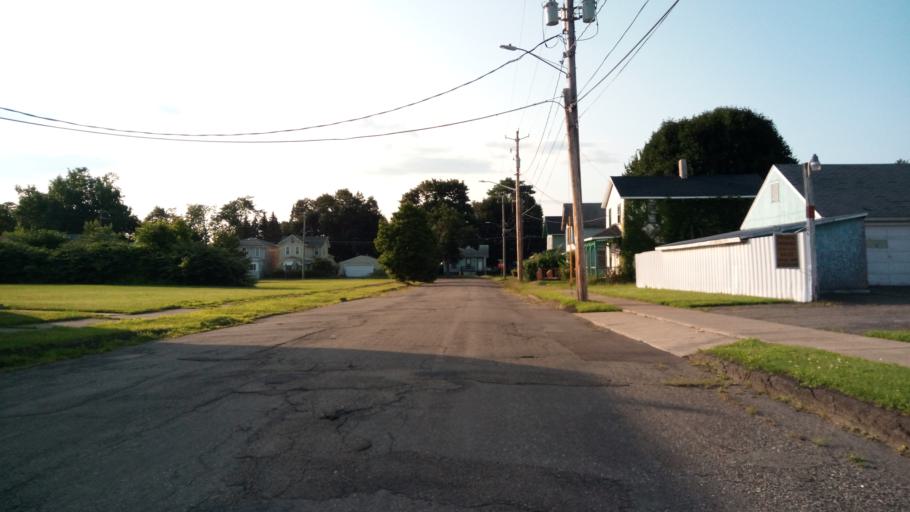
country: US
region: New York
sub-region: Chemung County
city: Elmira
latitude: 42.0937
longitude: -76.7967
